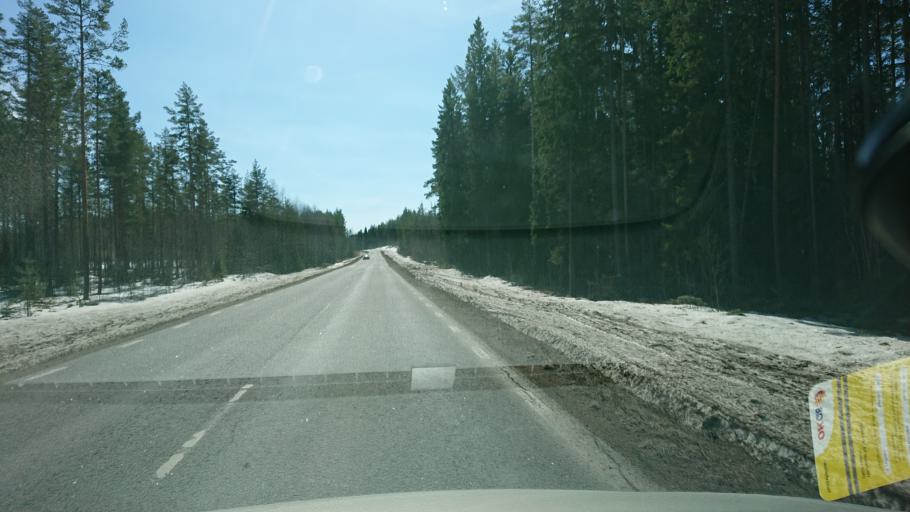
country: SE
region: Vaesternorrland
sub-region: Solleftea Kommun
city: As
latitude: 63.5974
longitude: 16.4280
